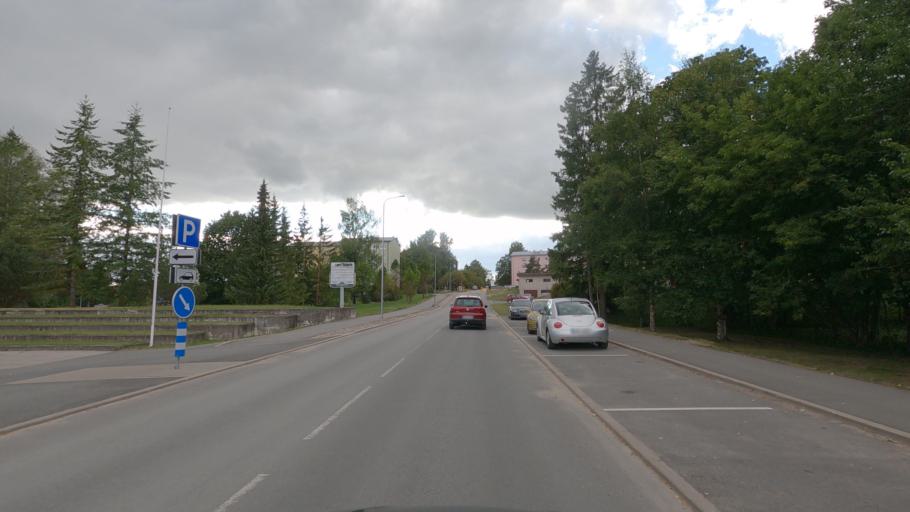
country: EE
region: Raplamaa
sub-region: Rapla vald
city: Rapla
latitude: 58.9989
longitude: 24.7983
